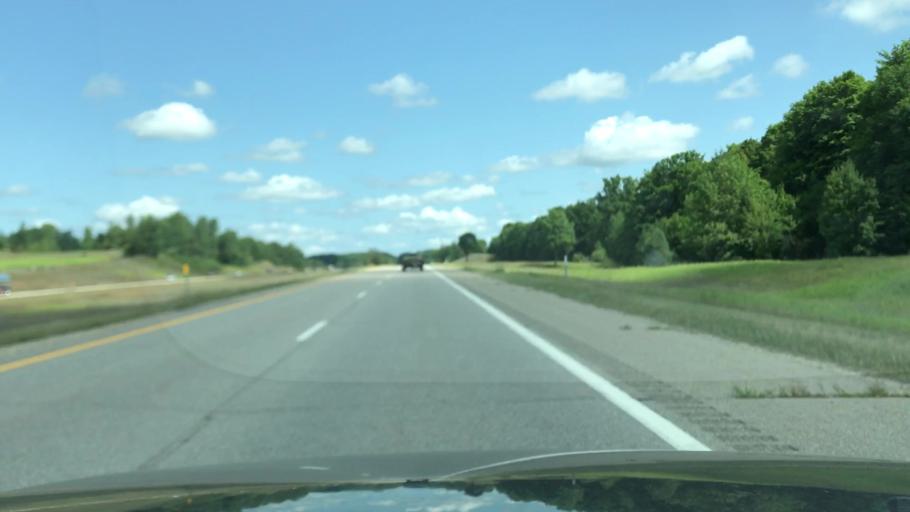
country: US
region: Michigan
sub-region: Osceola County
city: Reed City
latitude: 43.7916
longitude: -85.5337
